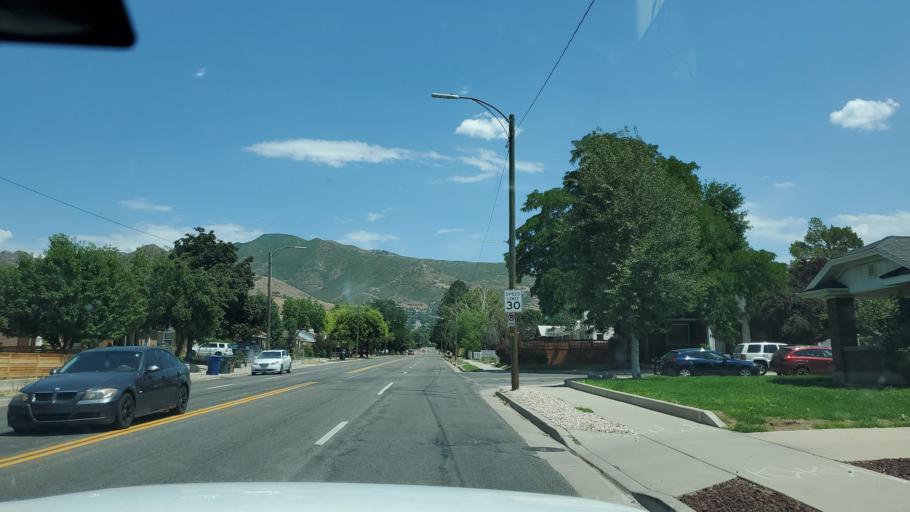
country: US
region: Utah
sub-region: Salt Lake County
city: Willard
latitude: 40.7255
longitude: -111.8361
